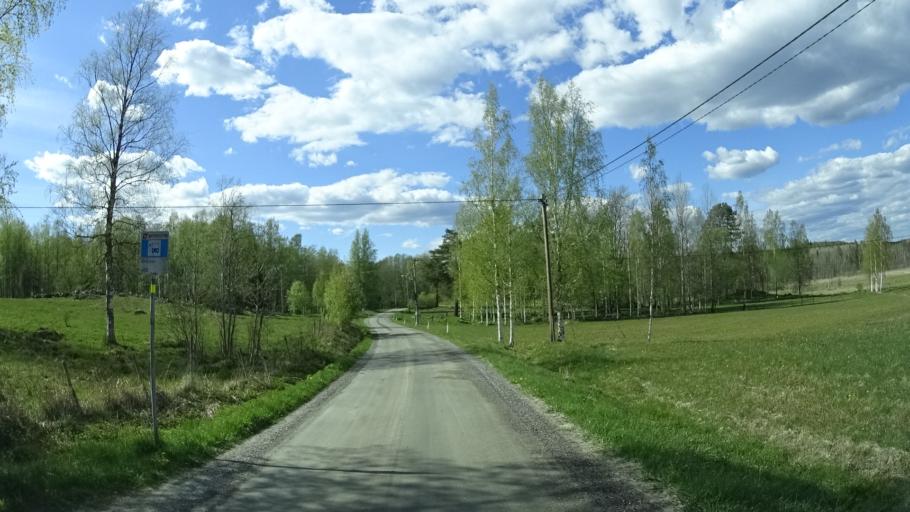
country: SE
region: OErebro
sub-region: Orebro Kommun
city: Garphyttan
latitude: 59.4419
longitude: 14.8196
